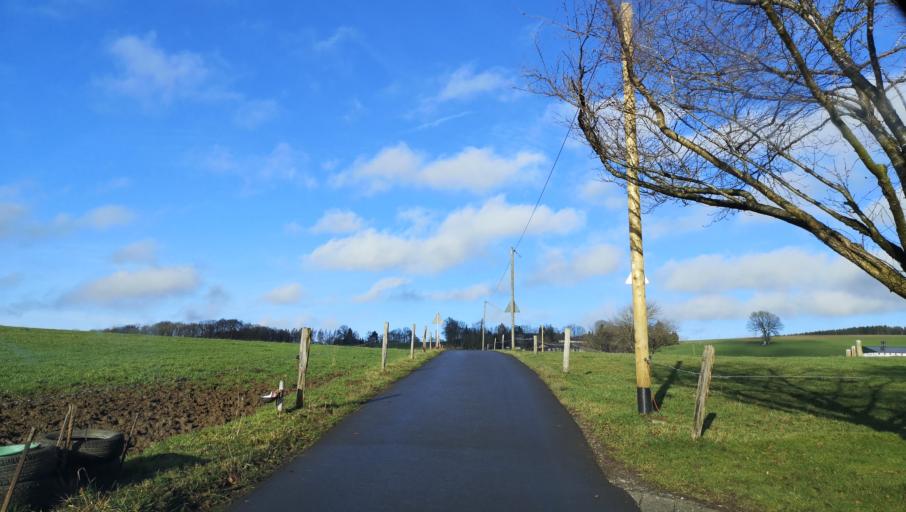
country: DE
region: North Rhine-Westphalia
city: Radevormwald
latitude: 51.1768
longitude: 7.4055
